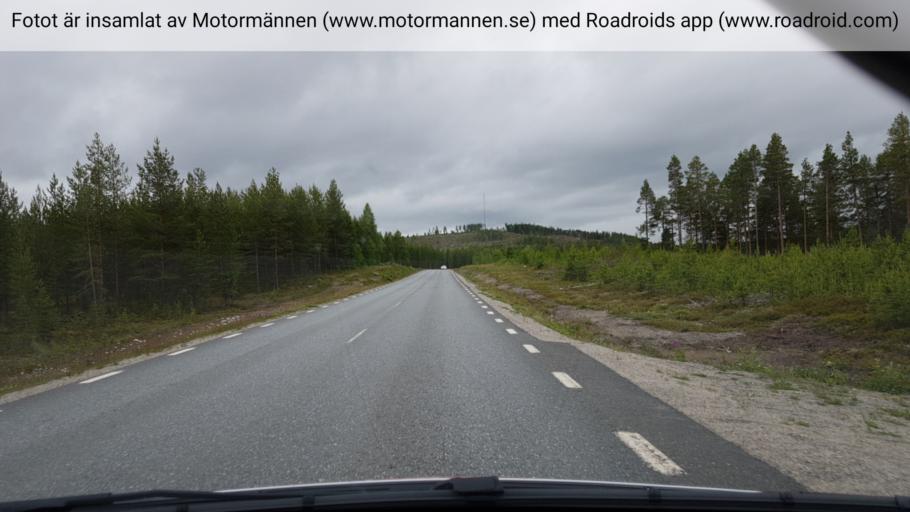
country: SE
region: Vaesterbotten
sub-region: Lycksele Kommun
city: Lycksele
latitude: 64.4817
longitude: 18.9005
